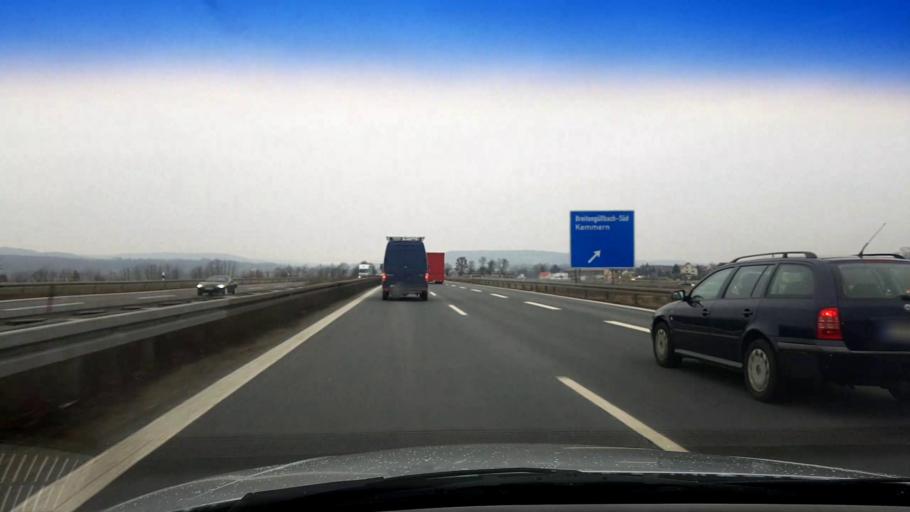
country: DE
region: Bavaria
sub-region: Upper Franconia
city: Kemmern
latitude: 49.9560
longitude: 10.8791
